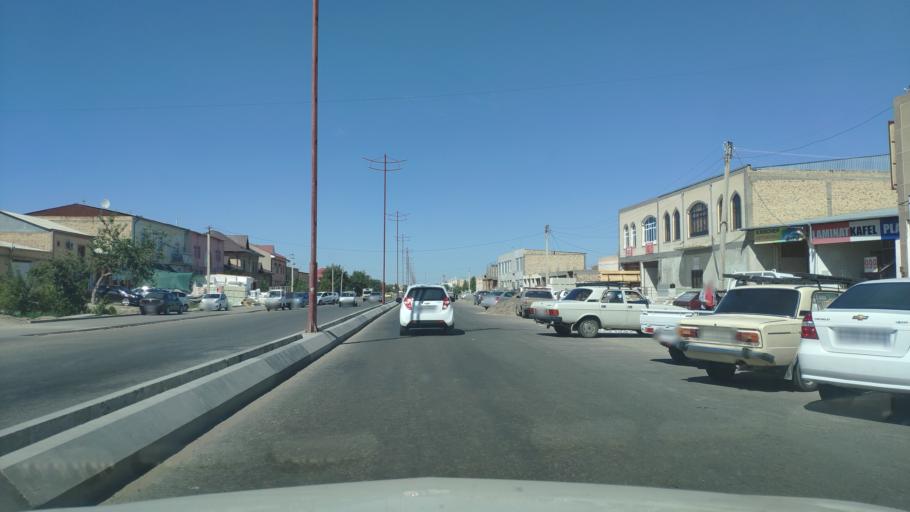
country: UZ
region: Bukhara
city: Bukhara
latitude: 39.7738
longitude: 64.3875
